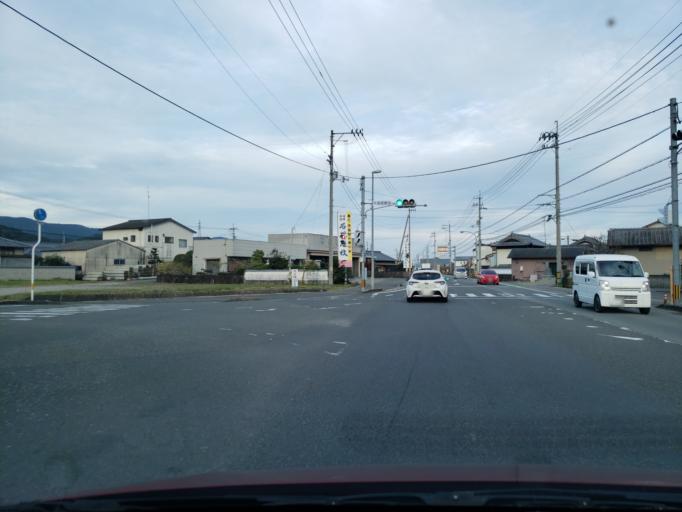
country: JP
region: Tokushima
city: Kamojimacho-jogejima
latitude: 34.0907
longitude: 134.3028
